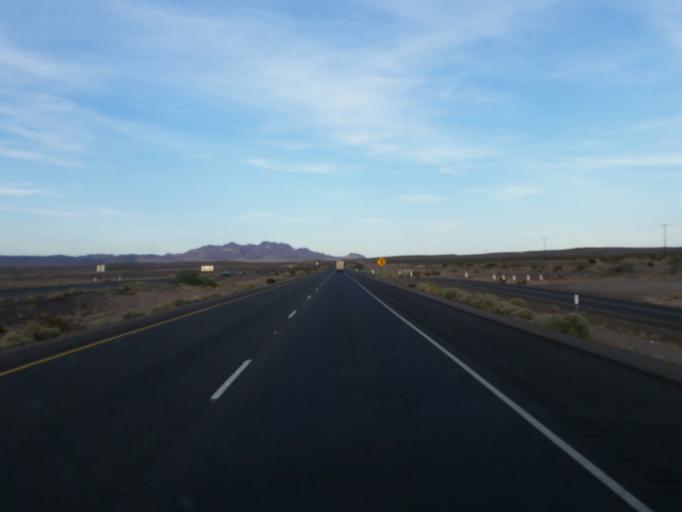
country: US
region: California
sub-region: San Bernardino County
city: Fort Irwin
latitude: 34.7877
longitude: -116.4517
